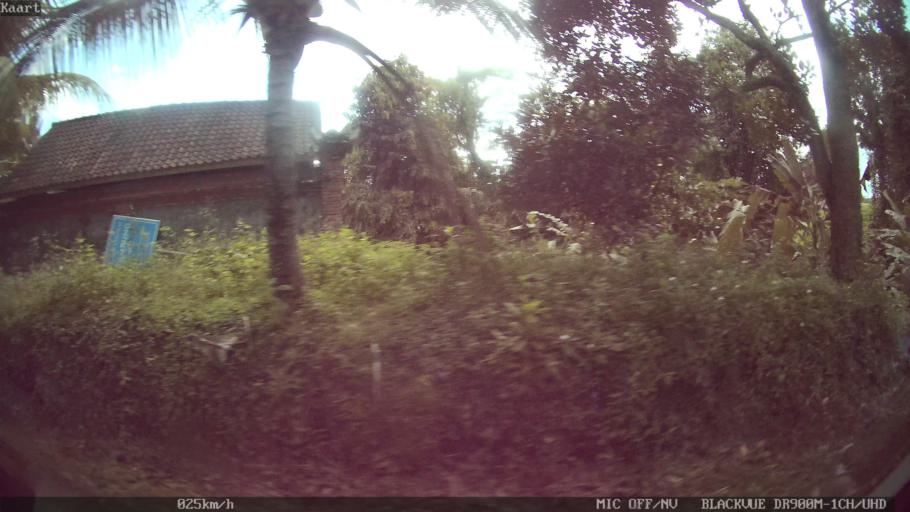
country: ID
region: Bali
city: Banjar Pesalakan
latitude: -8.5122
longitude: 115.3059
